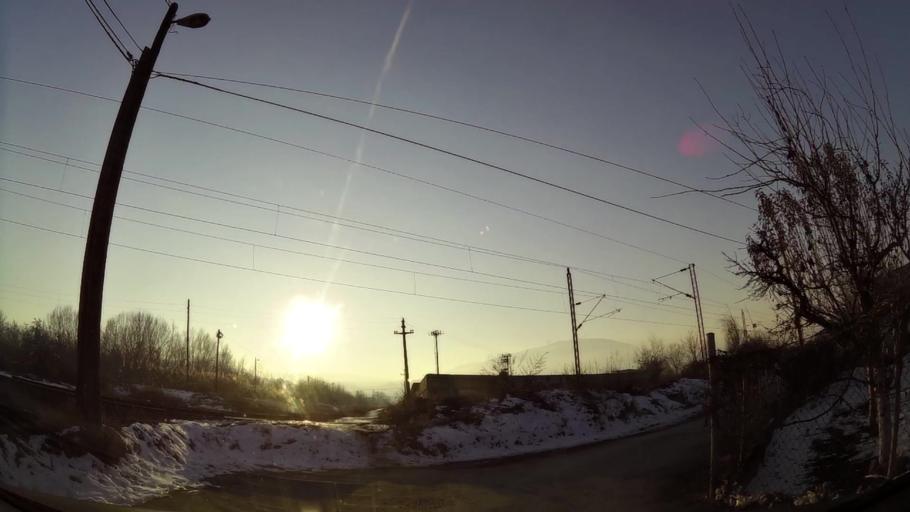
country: MK
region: Kisela Voda
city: Usje
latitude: 41.9700
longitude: 21.4734
